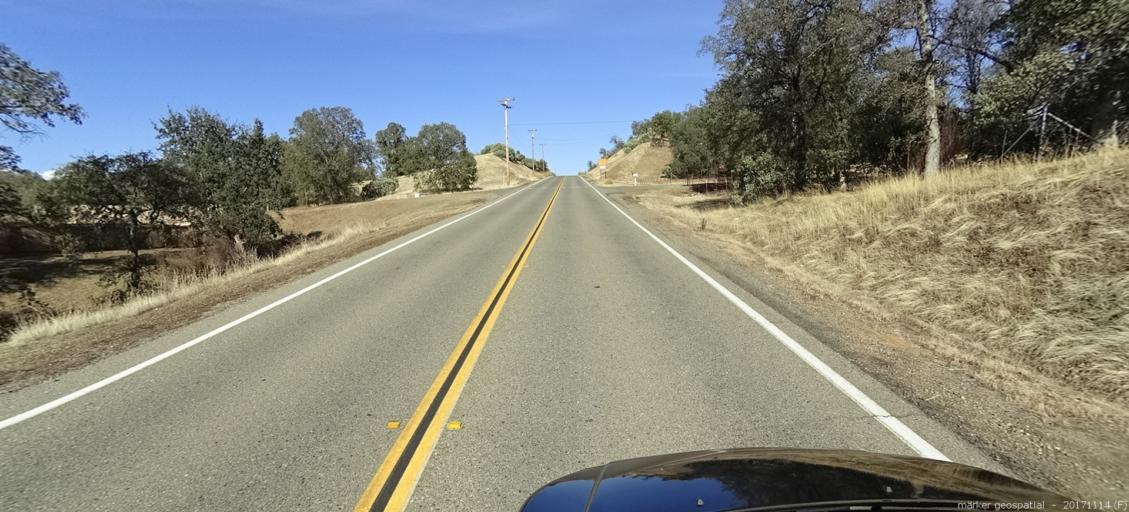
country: US
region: California
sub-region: Shasta County
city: Anderson
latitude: 40.4045
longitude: -122.4063
